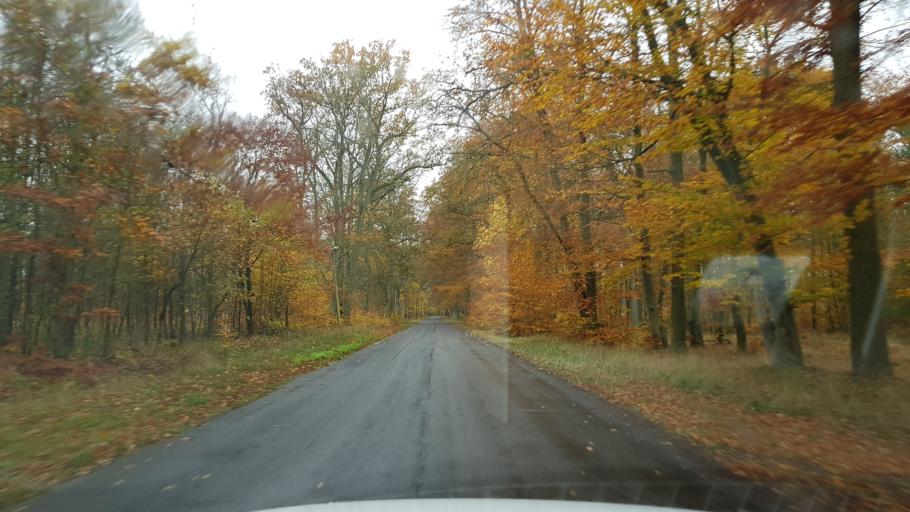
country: PL
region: West Pomeranian Voivodeship
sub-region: Powiat goleniowski
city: Stepnica
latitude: 53.6545
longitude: 14.6763
